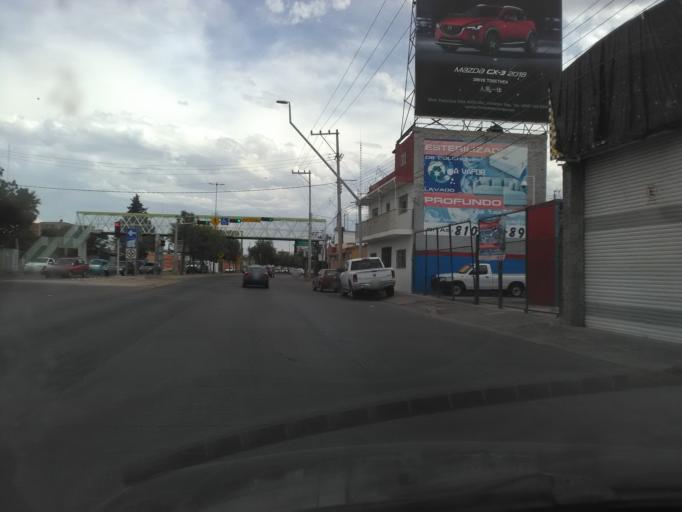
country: MX
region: Durango
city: Victoria de Durango
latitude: 24.0156
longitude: -104.6636
